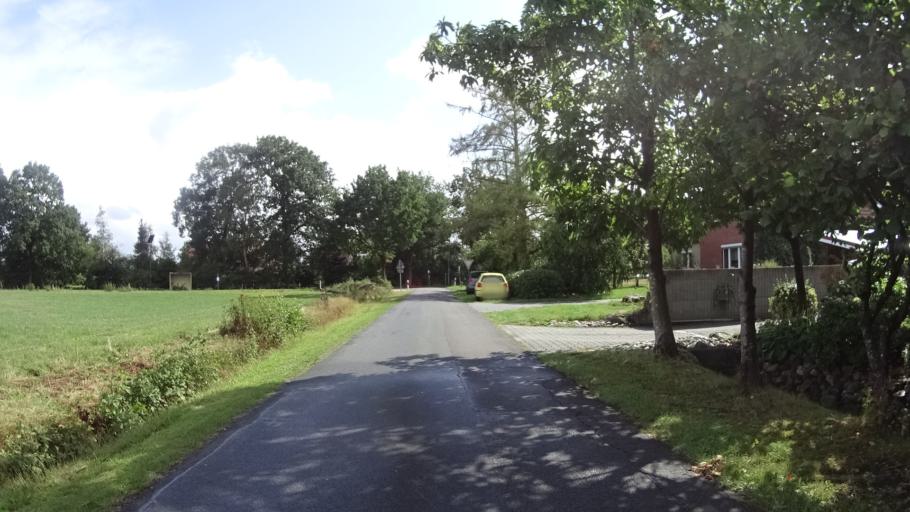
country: DE
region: Lower Saxony
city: Friedeburg
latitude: 53.3829
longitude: 7.8902
